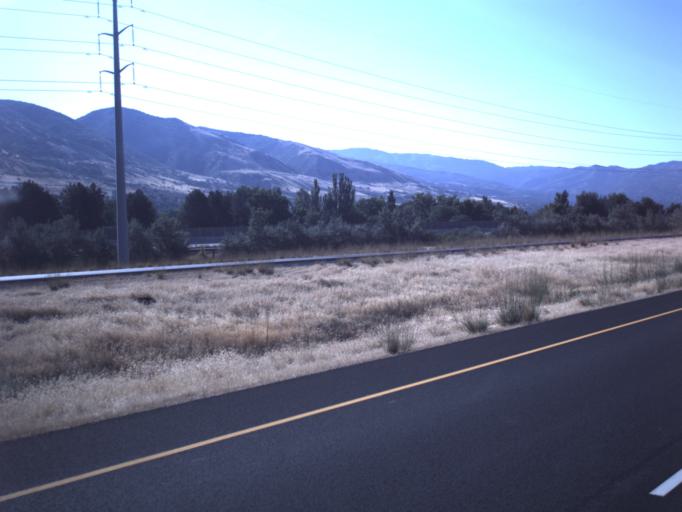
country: US
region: Utah
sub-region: Davis County
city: Farmington
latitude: 40.9472
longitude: -111.8930
